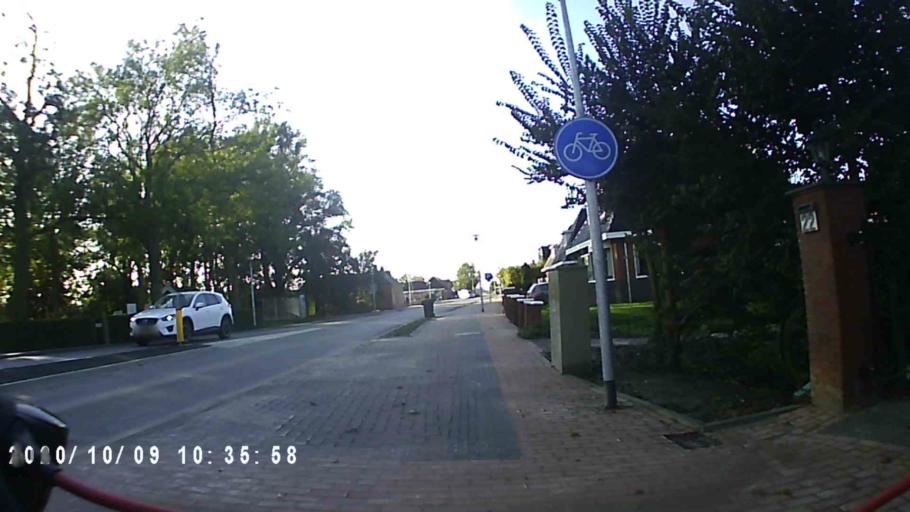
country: NL
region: Groningen
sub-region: Gemeente Winsum
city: Winsum
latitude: 53.2963
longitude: 6.5335
